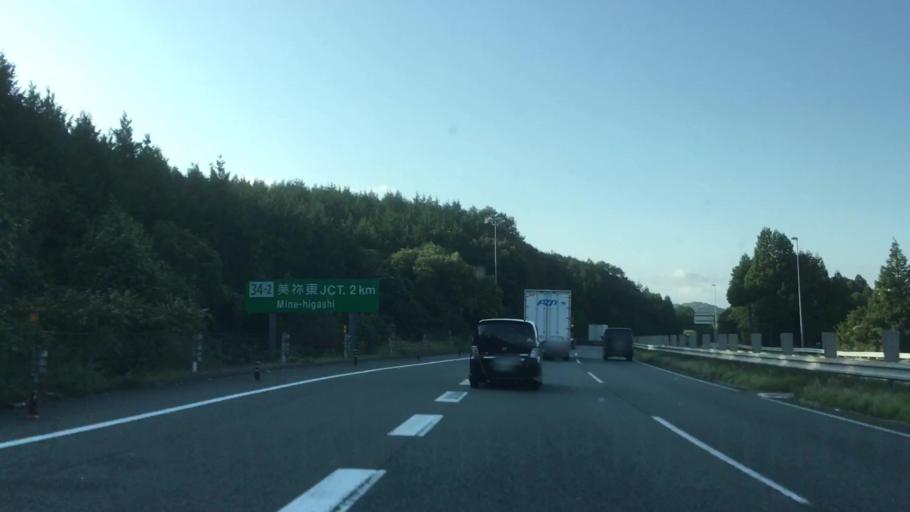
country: JP
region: Yamaguchi
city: Ogori-shimogo
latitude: 34.1552
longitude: 131.3343
